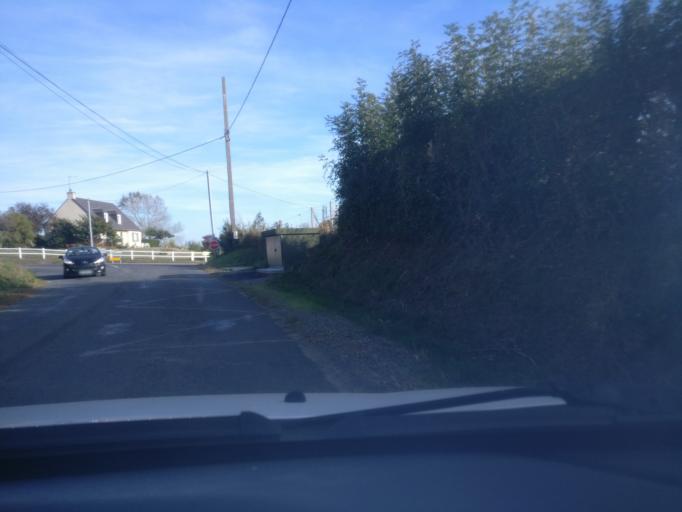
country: FR
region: Lower Normandy
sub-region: Departement de la Manche
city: Sartilly
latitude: 48.7080
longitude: -1.4730
